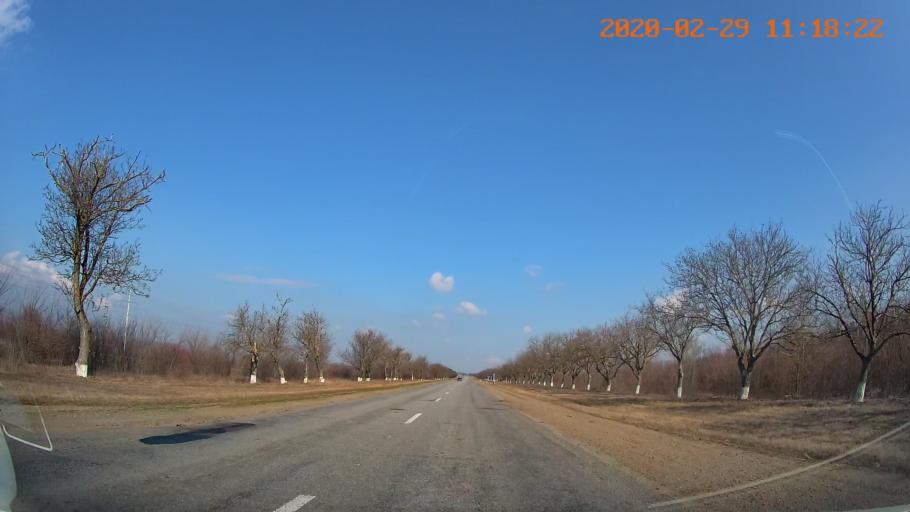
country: MD
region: Telenesti
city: Cocieri
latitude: 47.3340
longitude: 29.1730
